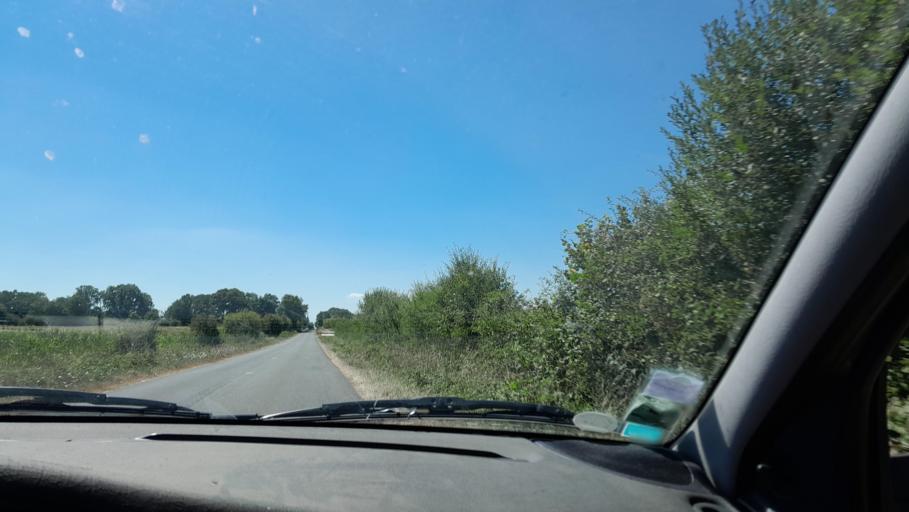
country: FR
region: Pays de la Loire
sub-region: Departement de la Mayenne
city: Congrier
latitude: 47.8327
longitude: -1.1760
